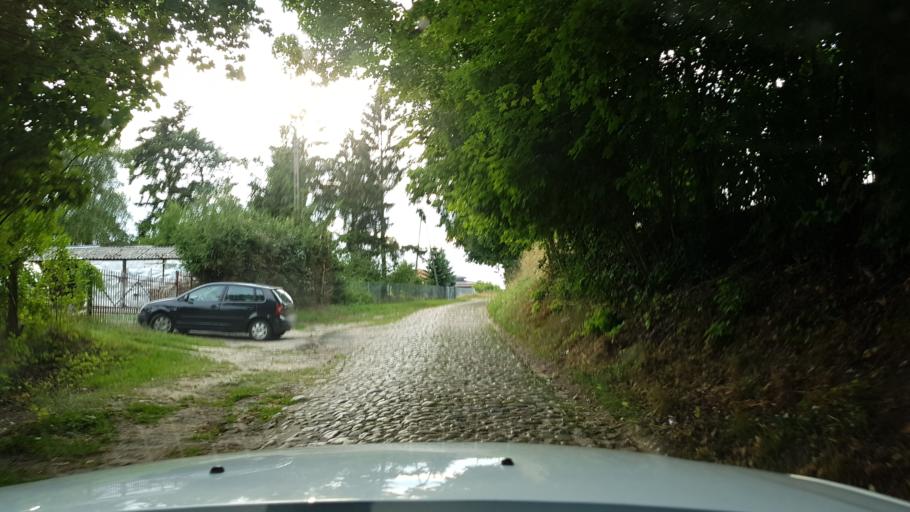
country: PL
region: West Pomeranian Voivodeship
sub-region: Powiat swidwinski
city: Polczyn-Zdroj
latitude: 53.7796
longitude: 16.0925
